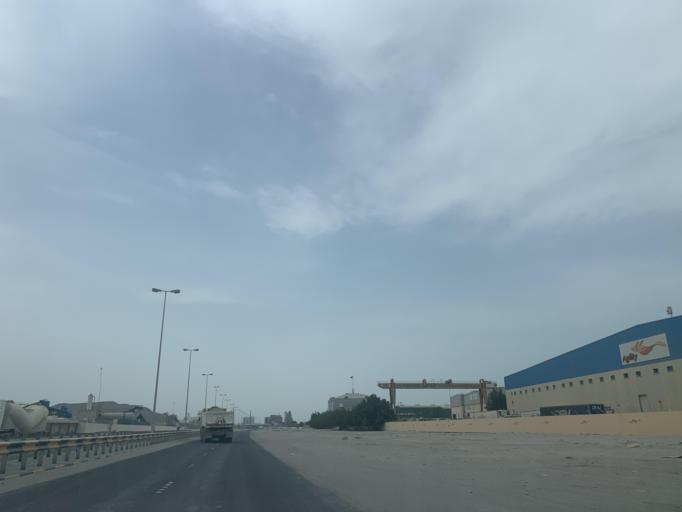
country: BH
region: Muharraq
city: Al Hadd
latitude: 26.2037
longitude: 50.6604
